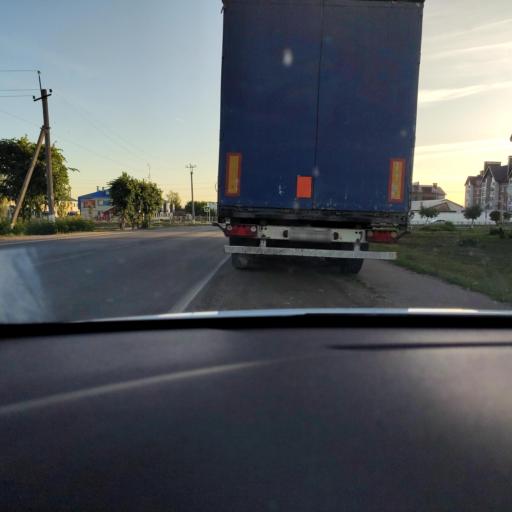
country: RU
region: Tatarstan
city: Pestretsy
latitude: 55.7566
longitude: 49.6523
